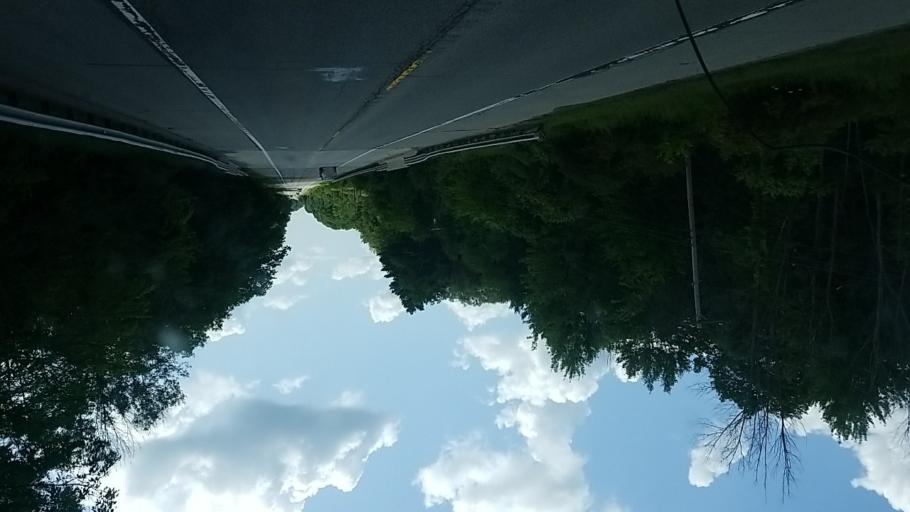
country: US
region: Michigan
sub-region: Muskegon County
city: Ravenna
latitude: 43.2353
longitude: -85.9045
